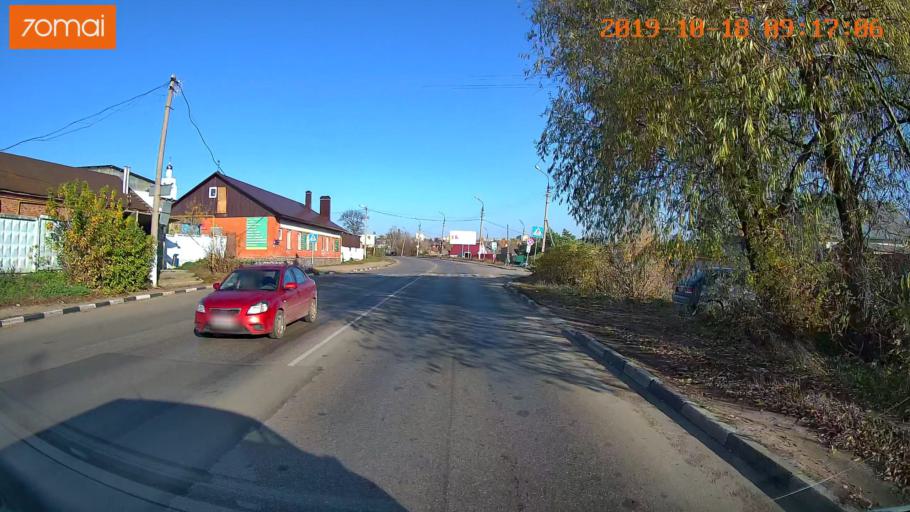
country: RU
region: Tula
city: Yefremov
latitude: 53.1324
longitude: 38.1162
